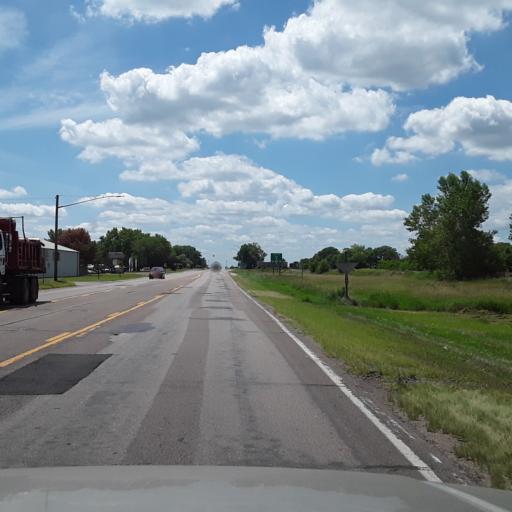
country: US
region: Nebraska
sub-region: Nance County
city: Genoa
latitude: 41.3141
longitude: -97.6672
